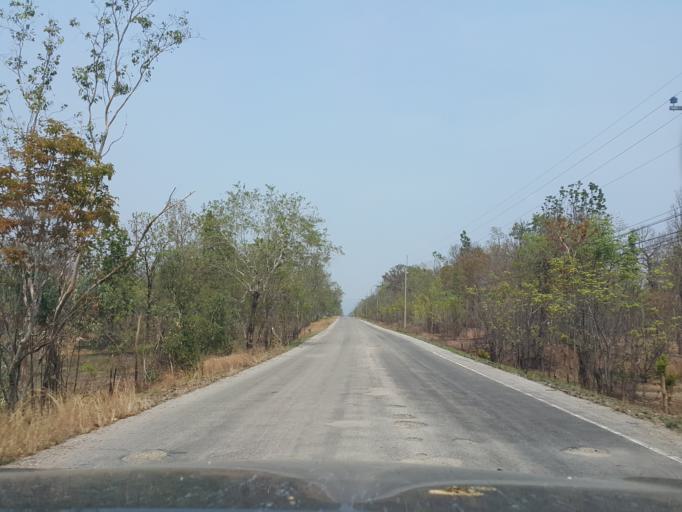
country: TH
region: Lampang
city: Mae Phrik
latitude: 17.5553
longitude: 99.1069
